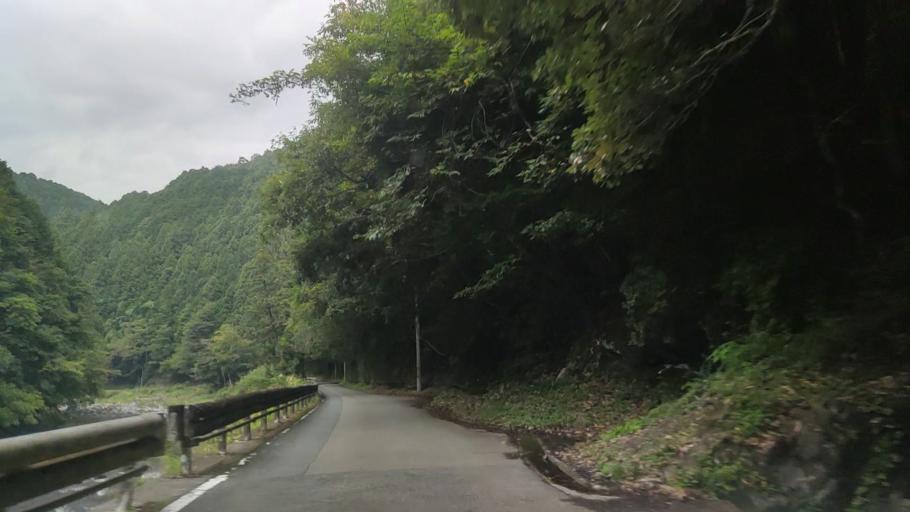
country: JP
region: Wakayama
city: Hashimoto
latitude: 34.2678
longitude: 135.6450
